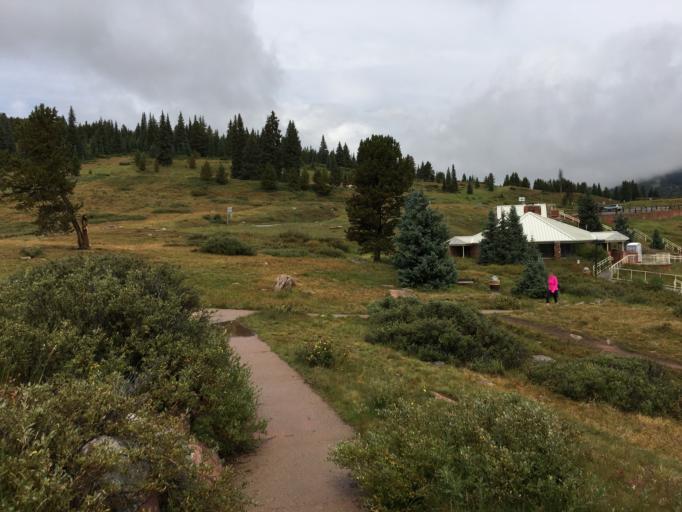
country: US
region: Colorado
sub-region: Summit County
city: Frisco
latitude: 39.5270
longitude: -106.2184
